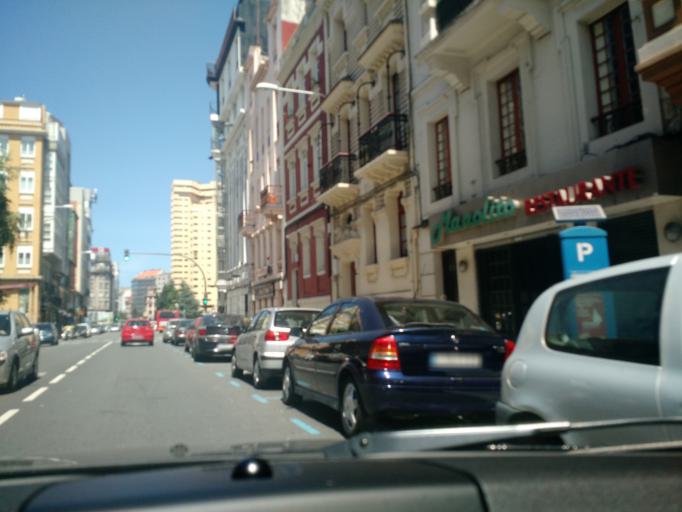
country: ES
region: Galicia
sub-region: Provincia da Coruna
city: A Coruna
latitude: 43.3554
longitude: -8.4048
